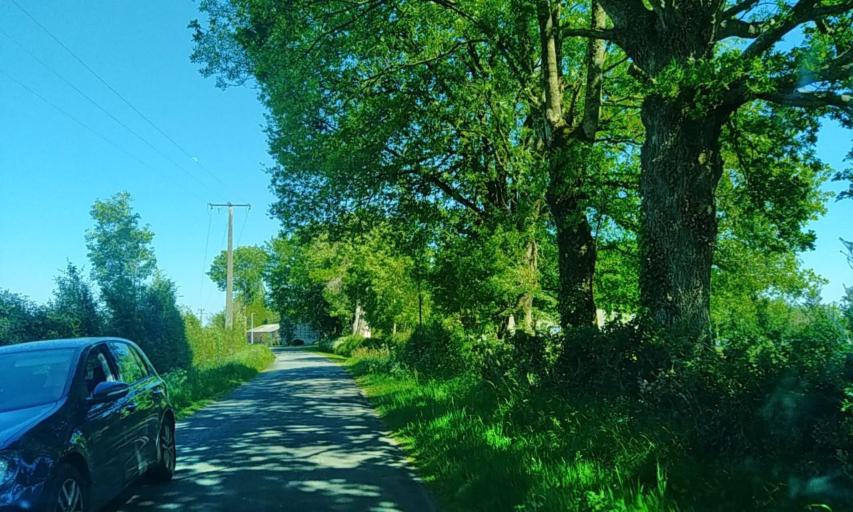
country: FR
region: Poitou-Charentes
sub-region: Departement des Deux-Sevres
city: Boisme
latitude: 46.7680
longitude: -0.4557
